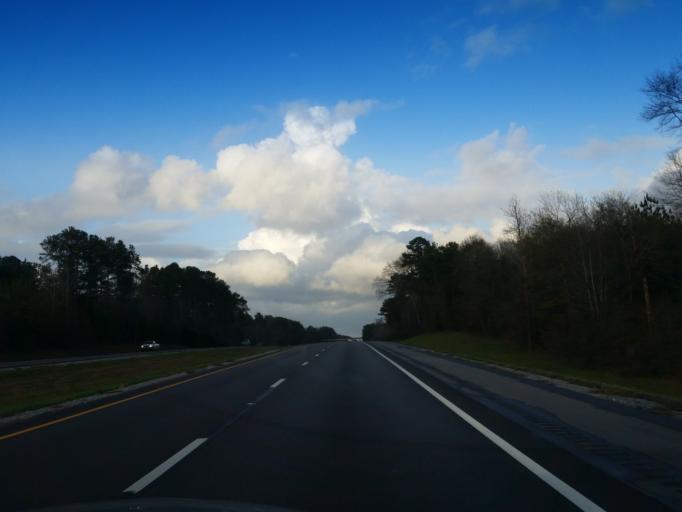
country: US
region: Mississippi
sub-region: Jones County
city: Sharon
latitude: 31.8773
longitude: -89.0430
